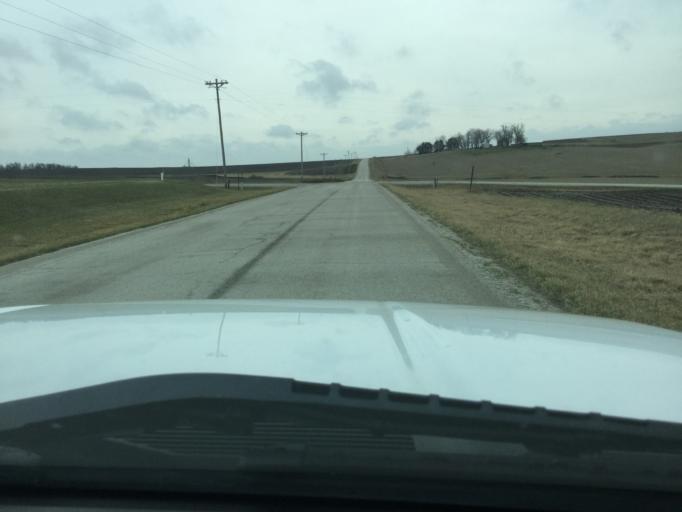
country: US
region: Kansas
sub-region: Nemaha County
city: Sabetha
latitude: 39.8984
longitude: -95.7137
